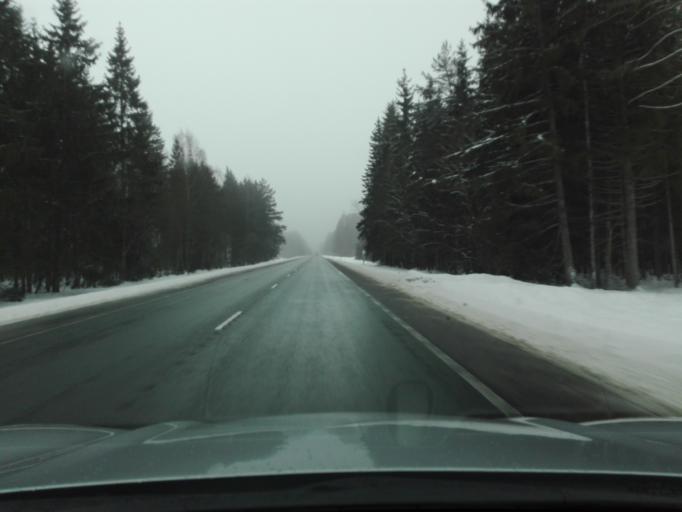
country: EE
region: Raplamaa
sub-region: Kohila vald
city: Kohila
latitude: 59.1577
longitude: 24.7758
